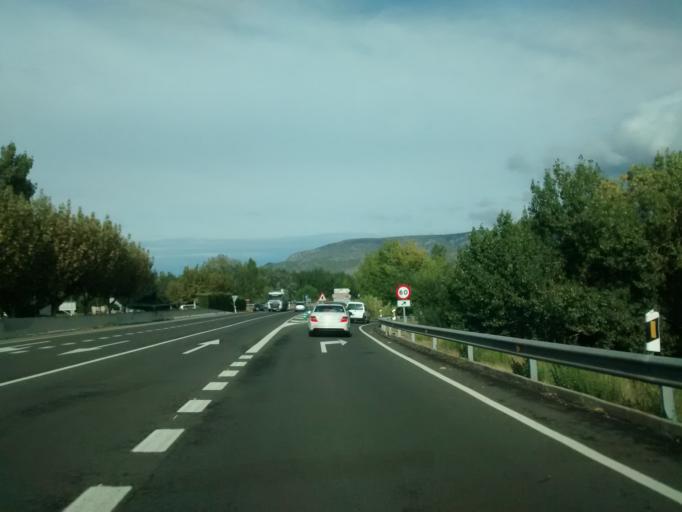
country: ES
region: Aragon
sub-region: Provincia de Huesca
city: Estada
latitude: 42.0655
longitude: 0.2045
